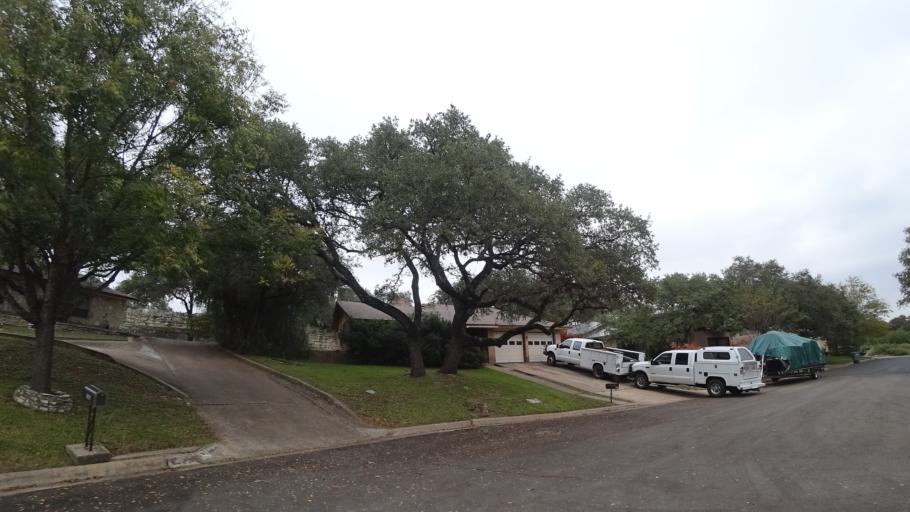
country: US
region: Texas
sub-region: Travis County
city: Barton Creek
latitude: 30.2382
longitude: -97.8844
